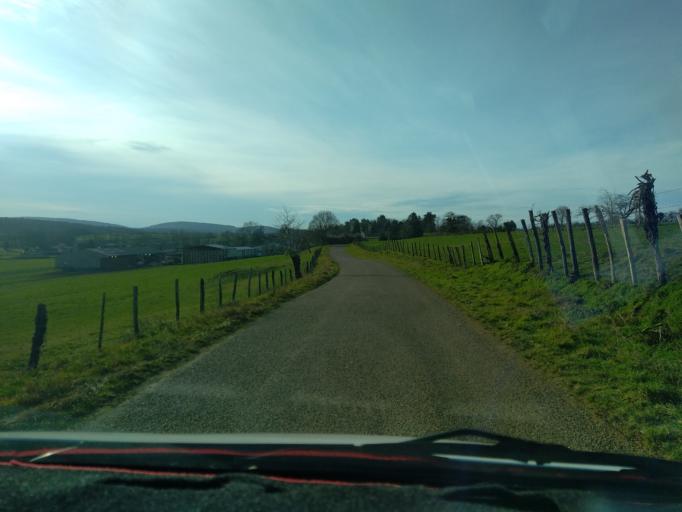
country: FR
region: Franche-Comte
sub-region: Departement de la Haute-Saone
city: Marnay
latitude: 47.3042
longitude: 5.6702
